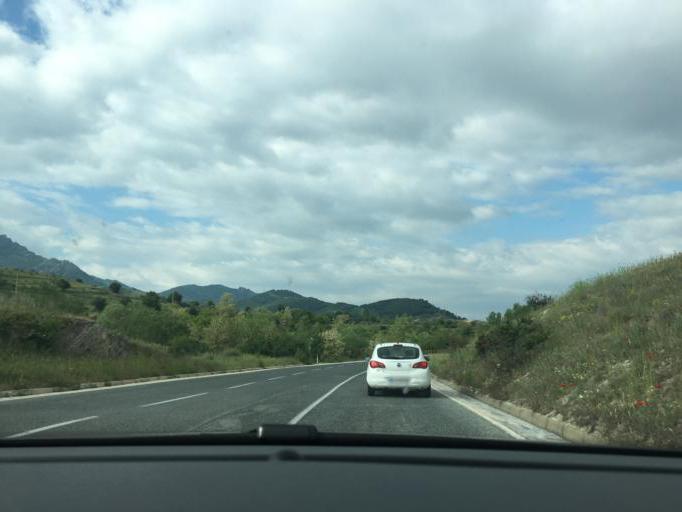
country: MK
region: Prilep
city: Prilep
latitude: 41.3656
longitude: 21.6086
